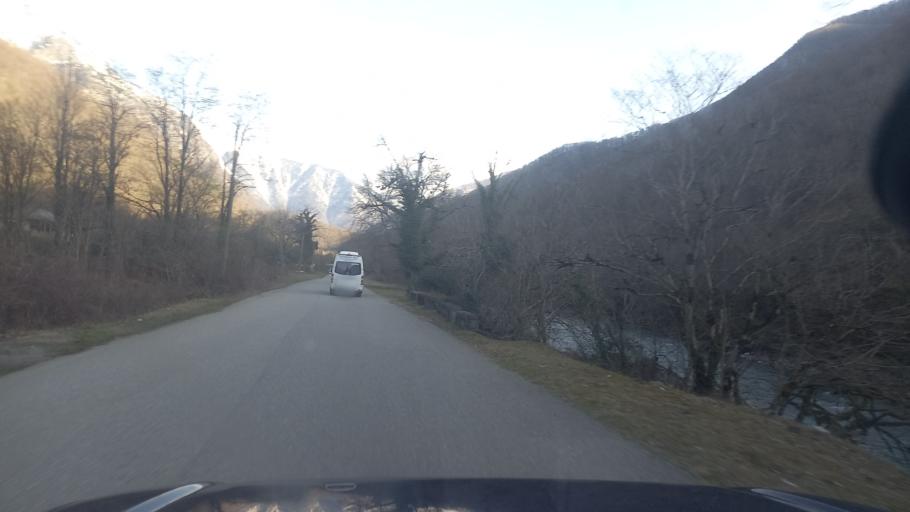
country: GE
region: Abkhazia
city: Gagra
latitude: 43.2841
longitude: 40.4001
